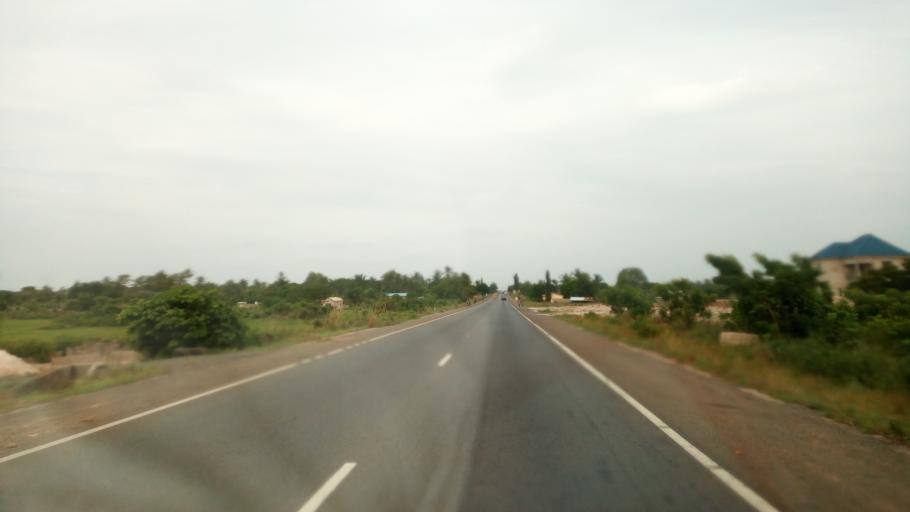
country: GH
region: Volta
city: Keta
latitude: 6.0558
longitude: 0.9846
